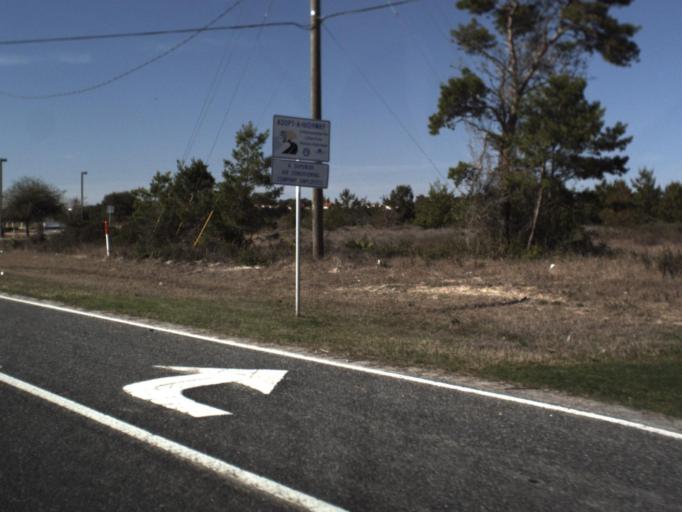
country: US
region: Florida
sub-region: Bay County
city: Laguna Beach
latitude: 30.2328
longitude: -85.8952
